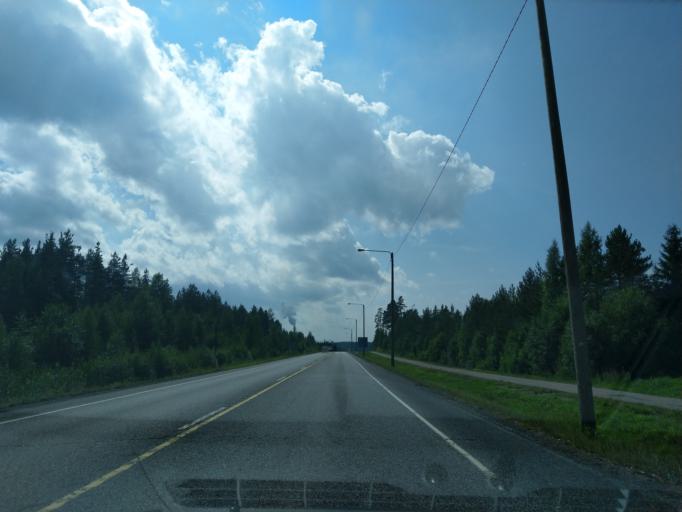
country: FI
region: South Karelia
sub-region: Imatra
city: Ruokolahti
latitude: 61.2638
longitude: 28.9137
